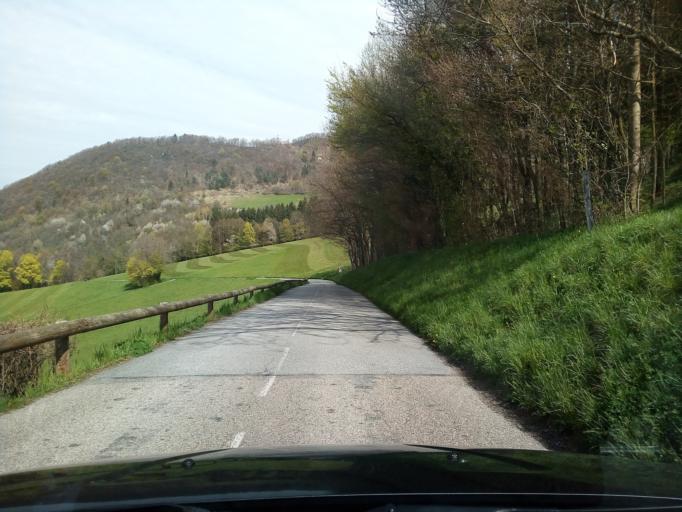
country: FR
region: Rhone-Alpes
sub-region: Departement de l'Isere
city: Herbeys
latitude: 45.1606
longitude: 5.8302
